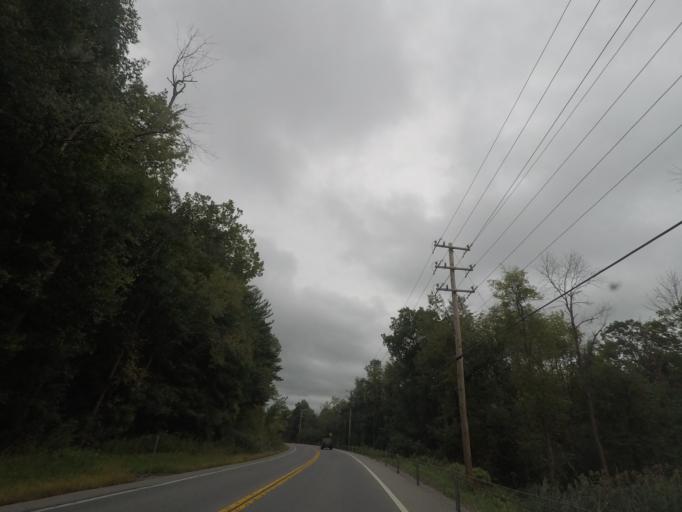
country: US
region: New York
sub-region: Saratoga County
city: Country Knolls
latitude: 42.9232
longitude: -73.7519
